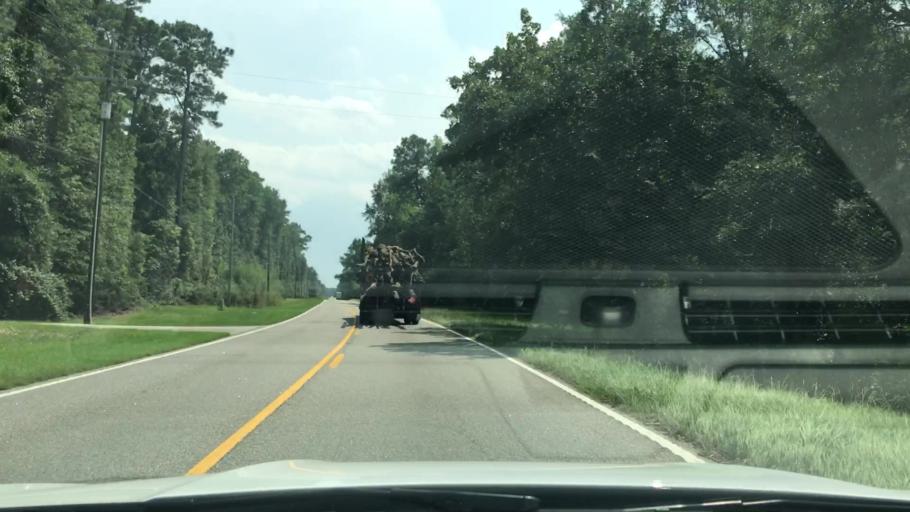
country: US
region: South Carolina
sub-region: Georgetown County
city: Georgetown
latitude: 33.4575
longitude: -79.2811
